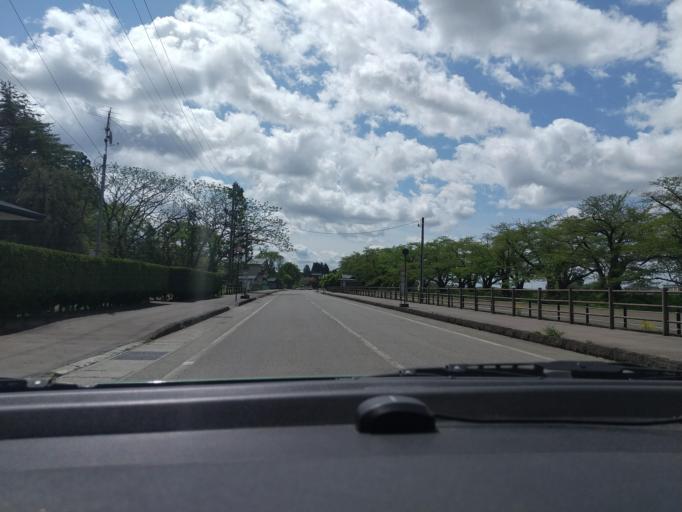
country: JP
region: Akita
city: Kakunodatemachi
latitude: 39.5990
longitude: 140.5601
